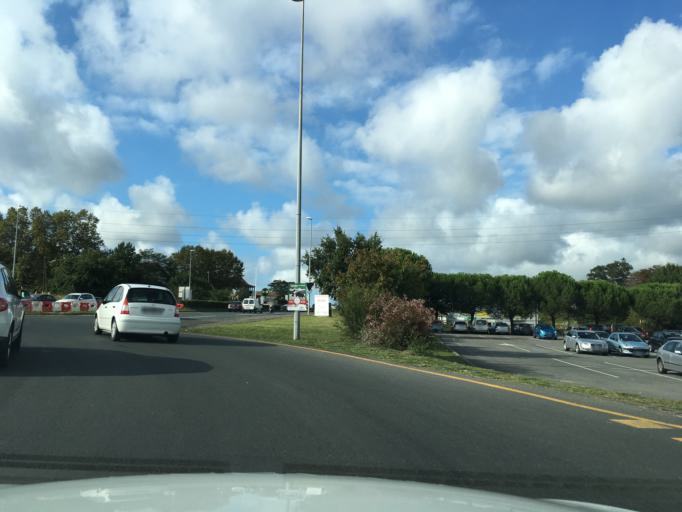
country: FR
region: Aquitaine
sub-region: Departement des Pyrenees-Atlantiques
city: Anglet
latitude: 43.4626
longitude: -1.4955
